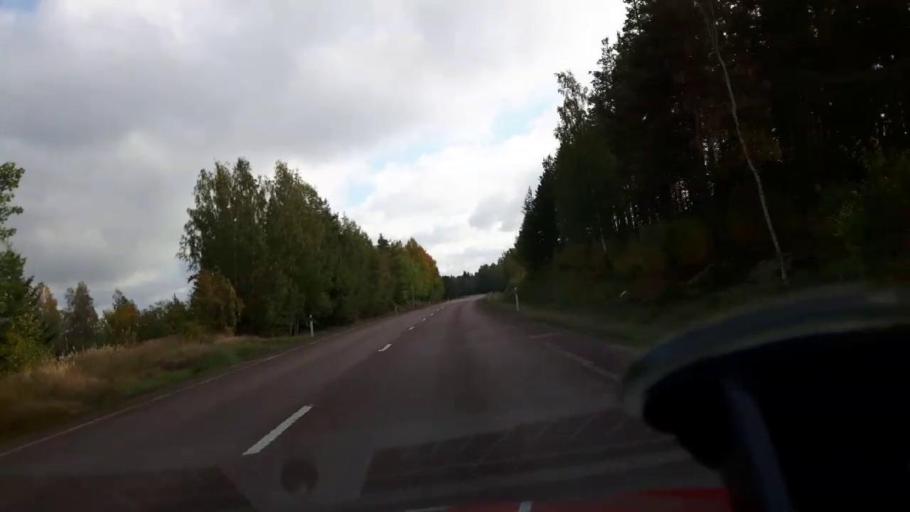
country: SE
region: Gaevleborg
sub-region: Ljusdals Kommun
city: Jaervsoe
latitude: 61.6475
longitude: 16.1983
